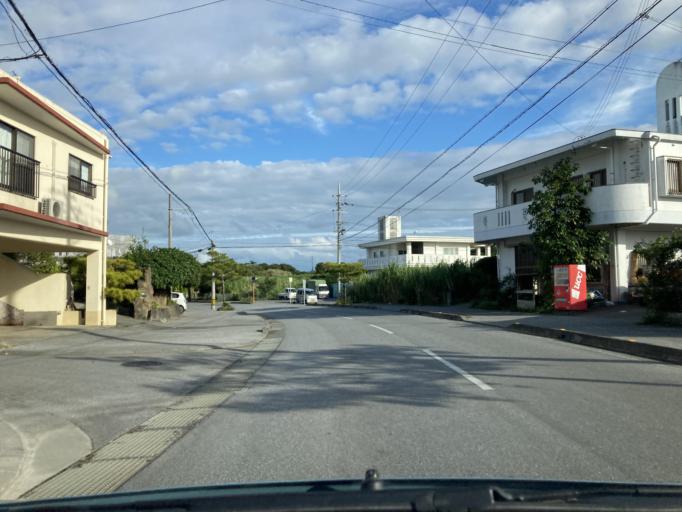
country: JP
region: Okinawa
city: Itoman
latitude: 26.1379
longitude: 127.7419
